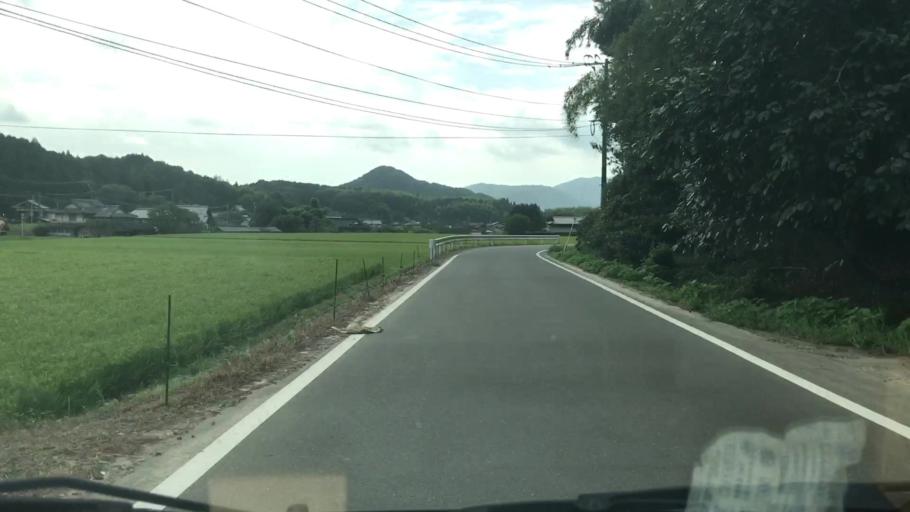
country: JP
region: Saga Prefecture
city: Takeocho-takeo
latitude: 33.2288
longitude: 130.0188
